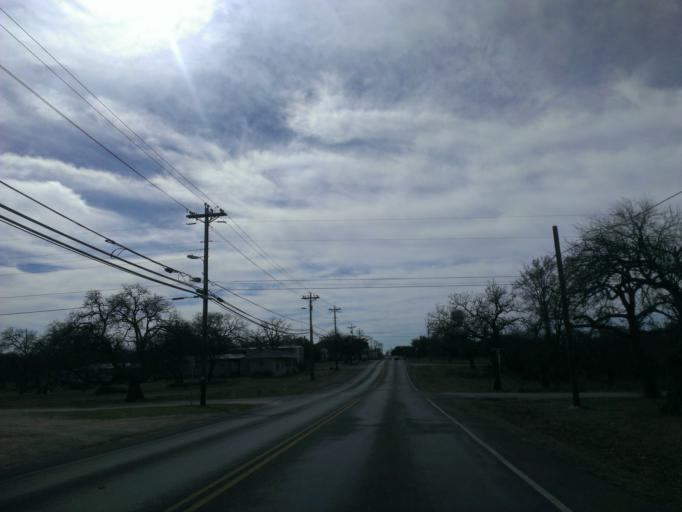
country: US
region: Texas
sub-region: Burnet County
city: Granite Shoals
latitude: 30.5927
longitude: -98.3841
